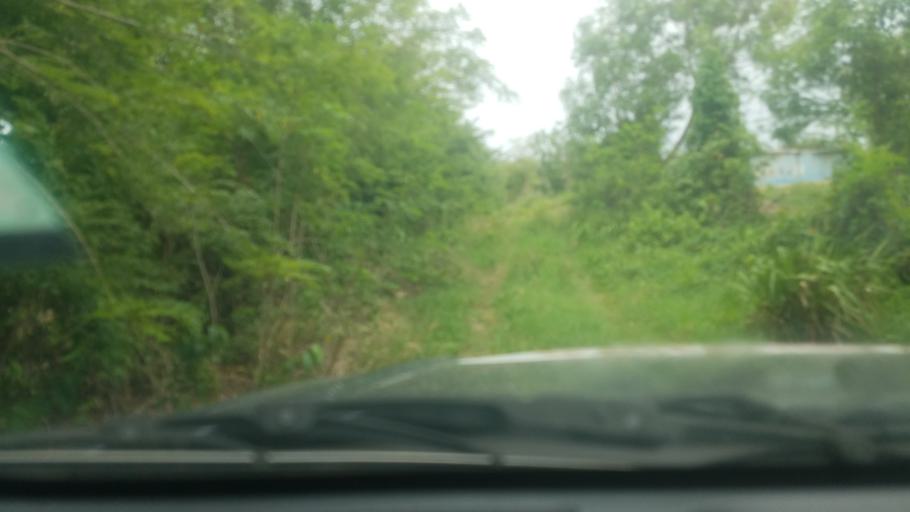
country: LC
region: Laborie Quarter
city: Laborie
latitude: 13.7463
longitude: -60.9784
